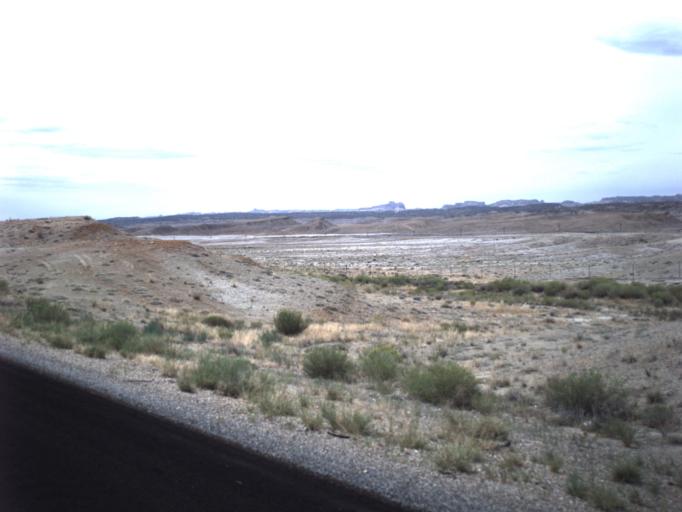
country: US
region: Utah
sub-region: Carbon County
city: East Carbon City
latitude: 39.1496
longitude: -110.3375
